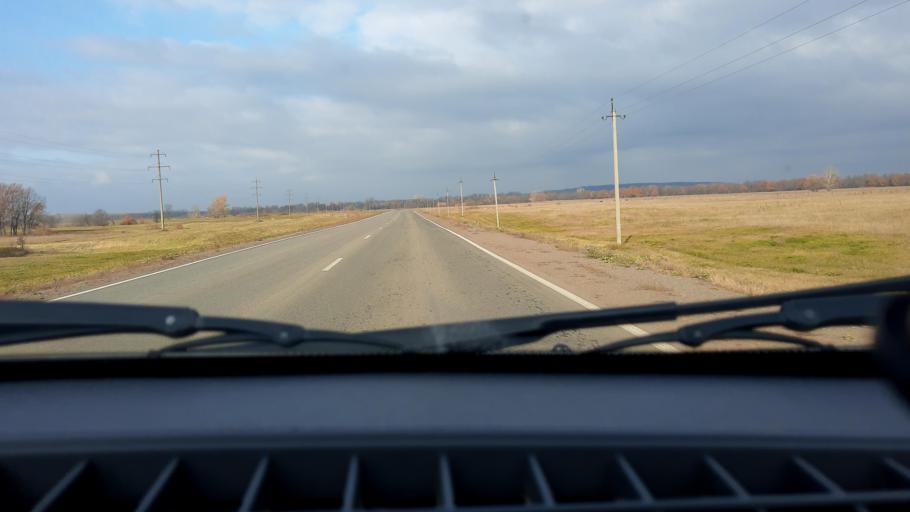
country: RU
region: Bashkortostan
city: Kabakovo
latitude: 54.5571
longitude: 56.0155
